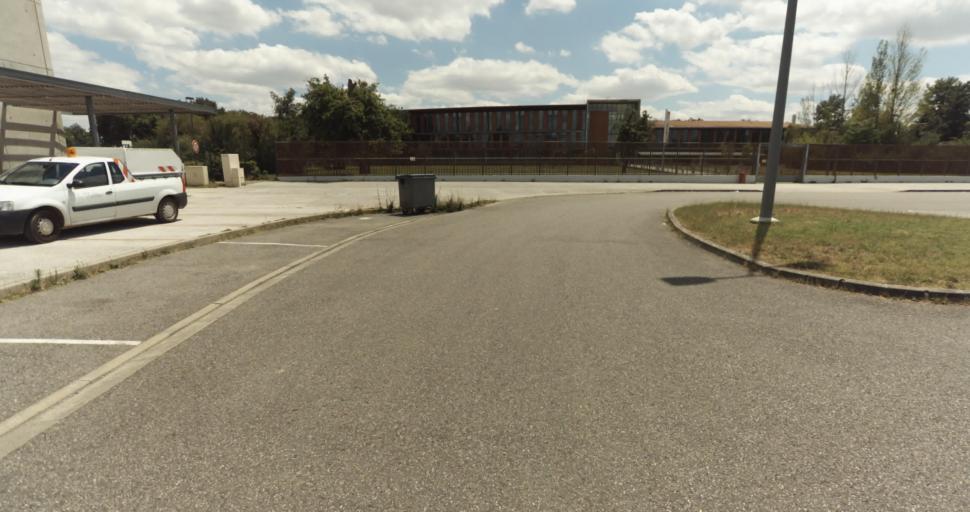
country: FR
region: Midi-Pyrenees
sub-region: Departement de la Haute-Garonne
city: Fontenilles
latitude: 43.5367
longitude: 1.1950
